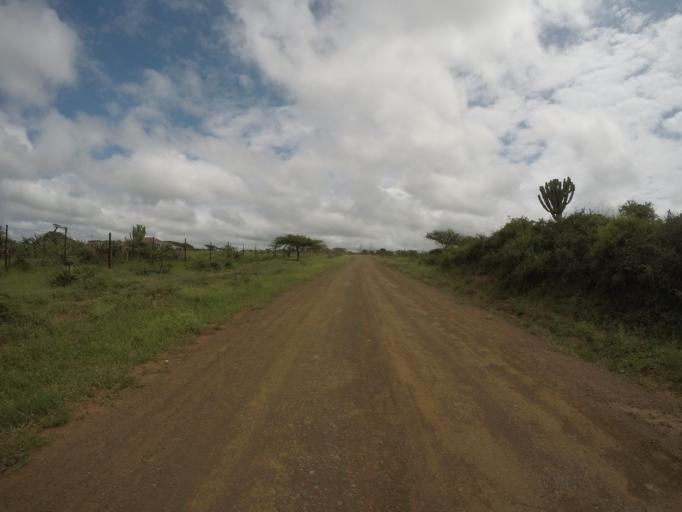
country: ZA
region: KwaZulu-Natal
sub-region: uThungulu District Municipality
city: Empangeni
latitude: -28.5822
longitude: 31.8522
